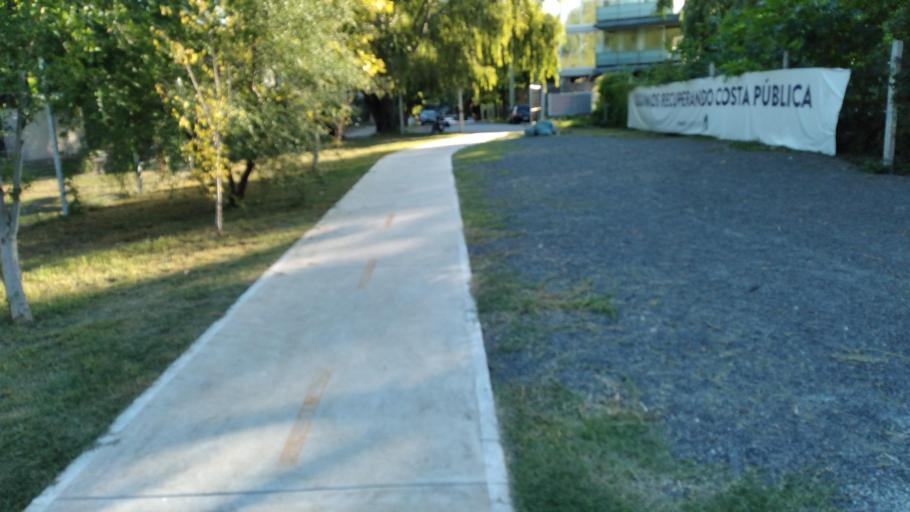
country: AR
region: Buenos Aires
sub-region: Partido de Vicente Lopez
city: Olivos
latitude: -34.4977
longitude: -58.4792
